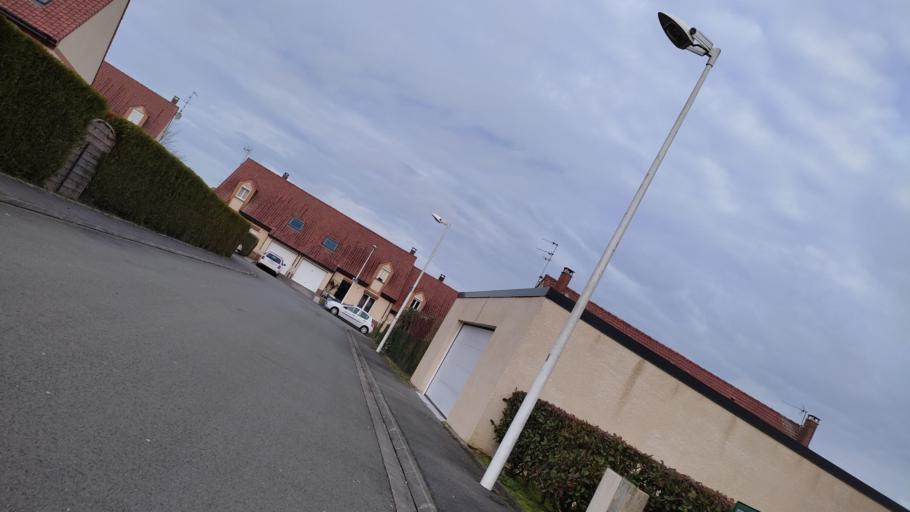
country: FR
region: Nord-Pas-de-Calais
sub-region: Departement du Pas-de-Calais
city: Anzin-Saint-Aubin
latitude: 50.3047
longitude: 2.7398
